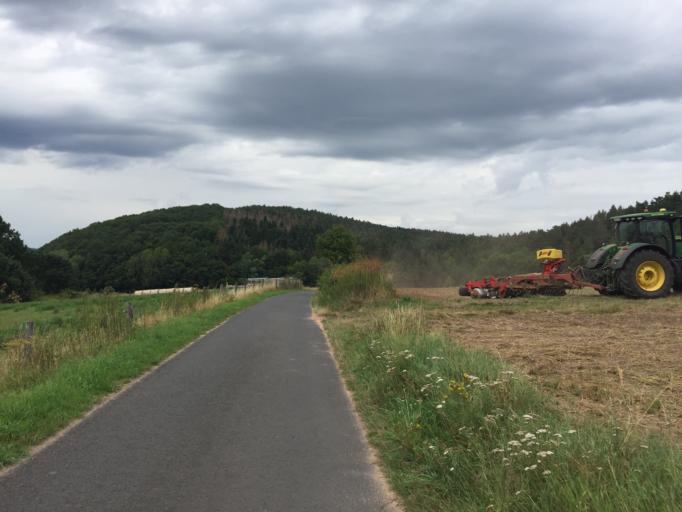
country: DE
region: Hesse
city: Breitenbach
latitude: 50.9329
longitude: 9.7910
